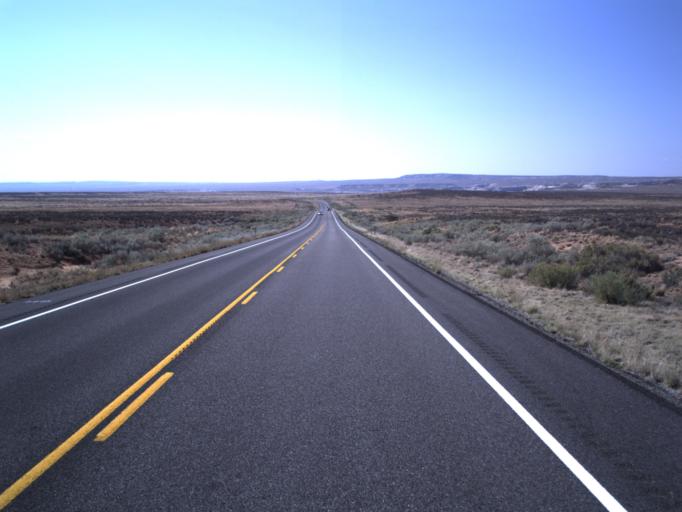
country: US
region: Utah
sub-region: San Juan County
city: Blanding
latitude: 37.3489
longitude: -109.5189
